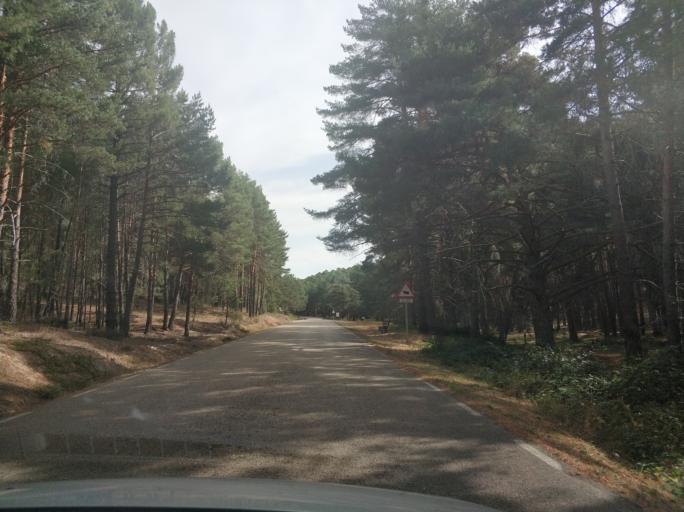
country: ES
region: Castille and Leon
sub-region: Provincia de Soria
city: Navaleno
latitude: 41.8422
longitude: -2.9973
